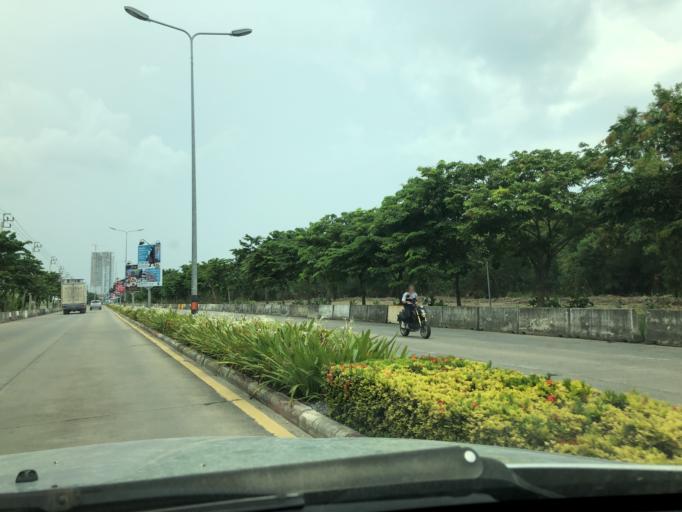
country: TH
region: Nonthaburi
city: Pak Kret
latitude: 13.9291
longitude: 100.5406
